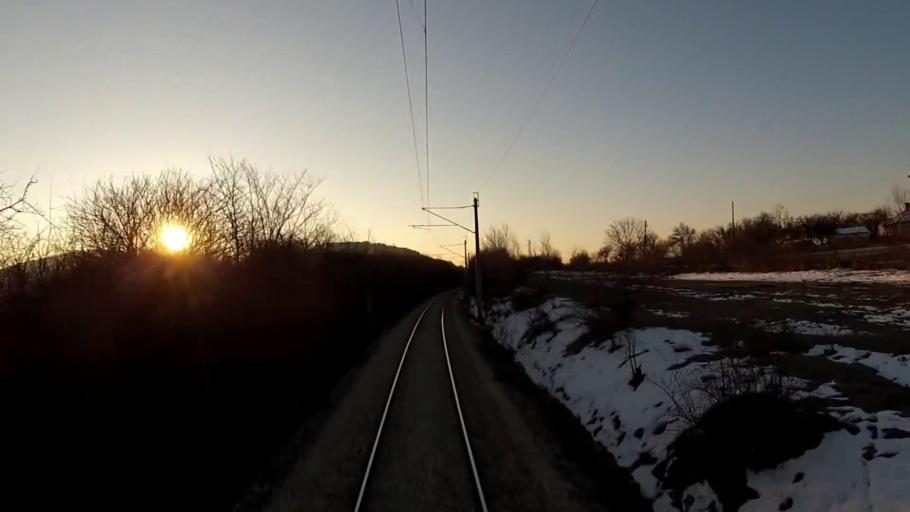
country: BG
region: Sofiya
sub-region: Obshtina Dragoman
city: Dragoman
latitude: 42.9078
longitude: 22.9448
